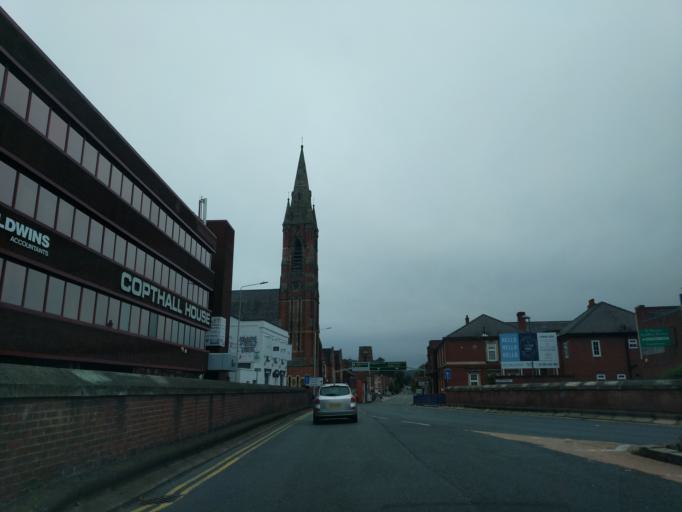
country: GB
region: England
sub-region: Dudley
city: Stourbridge
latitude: 52.4546
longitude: -2.1438
